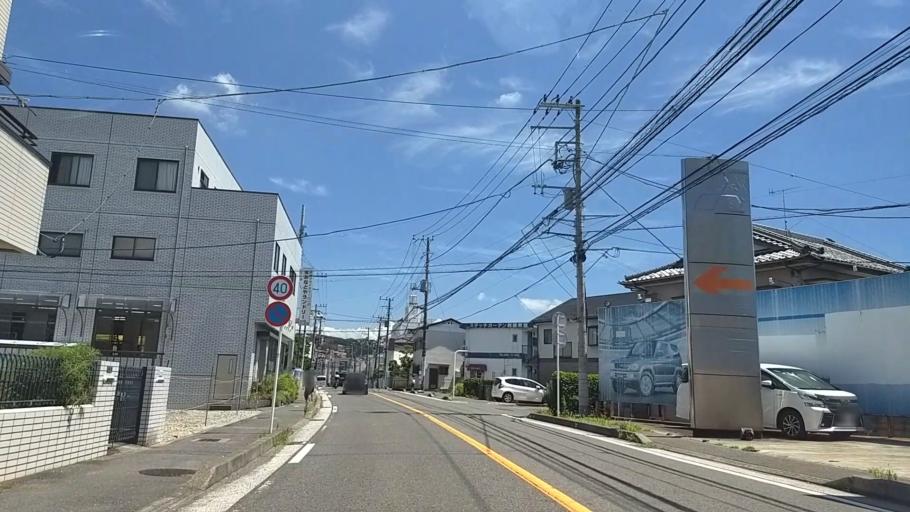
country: JP
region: Kanagawa
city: Zushi
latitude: 35.2984
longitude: 139.5721
